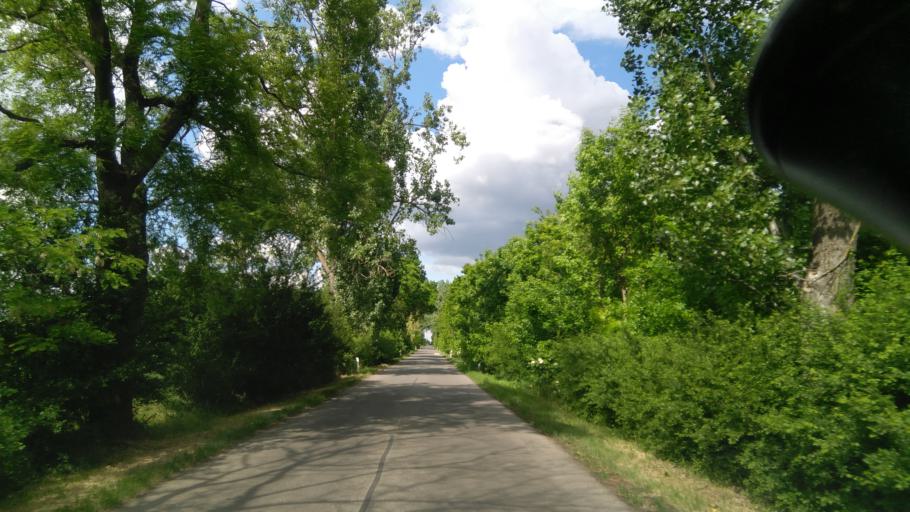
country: HU
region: Bekes
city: Bucsa
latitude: 47.1604
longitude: 21.0846
